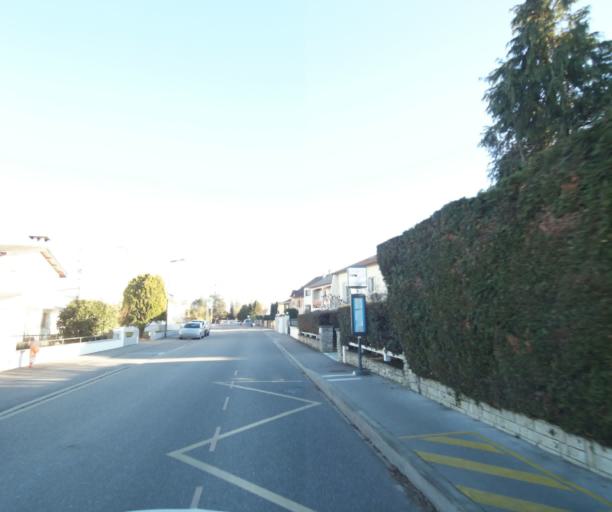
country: FR
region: Lorraine
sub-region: Departement de Meurthe-et-Moselle
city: Laneuveville-devant-Nancy
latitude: 48.6504
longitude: 6.2296
